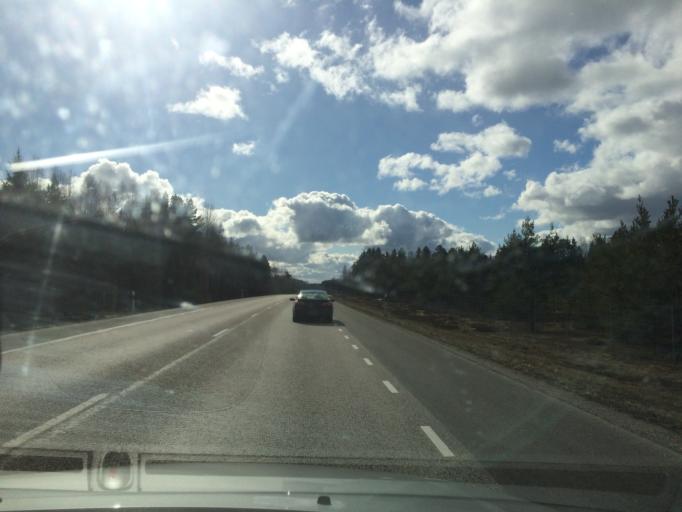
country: SE
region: Vaestra Goetaland
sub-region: Gotene Kommun
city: Goetene
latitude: 58.5841
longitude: 13.6147
